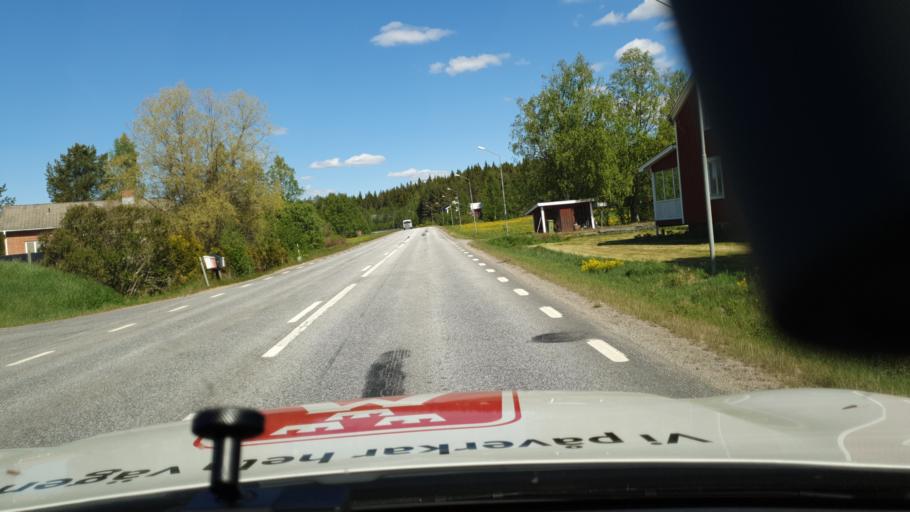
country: SE
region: Vaesterbotten
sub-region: Vannas Kommun
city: Vaennaes
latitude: 63.9611
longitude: 19.7526
